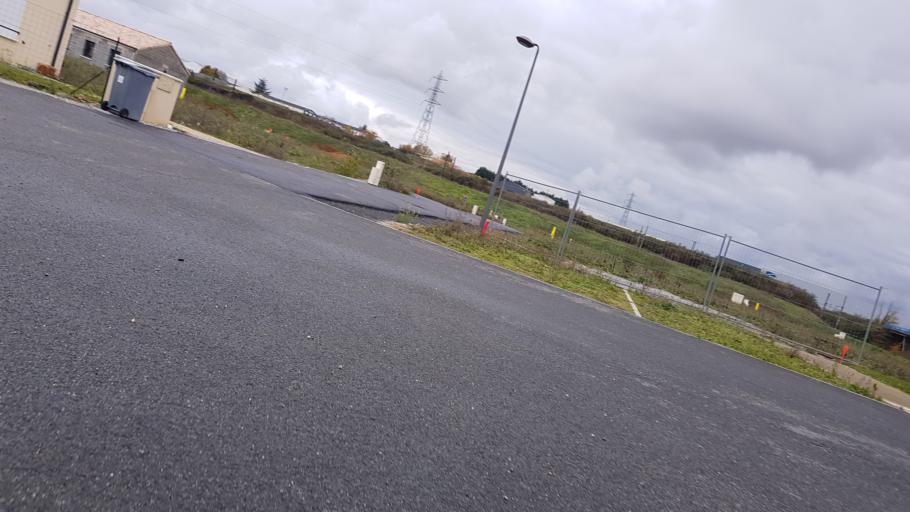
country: FR
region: Poitou-Charentes
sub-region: Departement de la Vienne
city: Chasseneuil-du-Poitou
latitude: 46.6626
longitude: 0.3802
